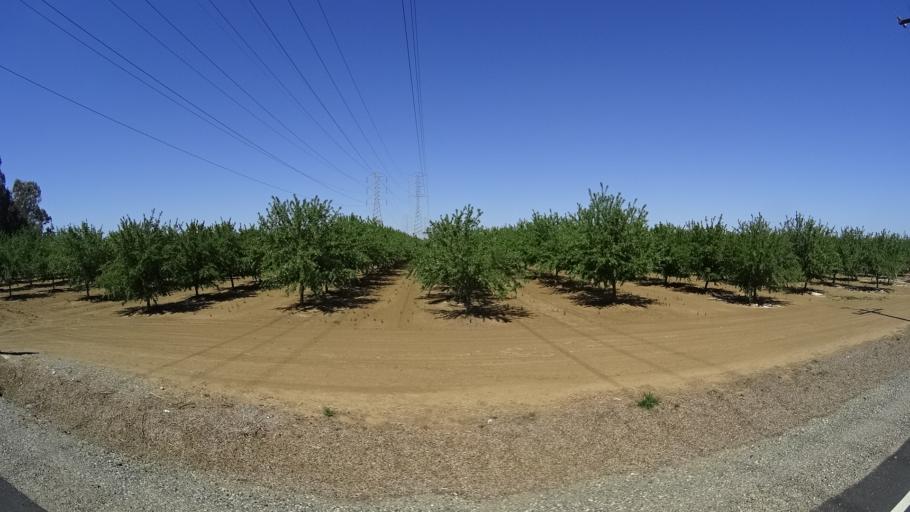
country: US
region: California
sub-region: Glenn County
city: Willows
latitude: 39.5241
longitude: -122.2635
